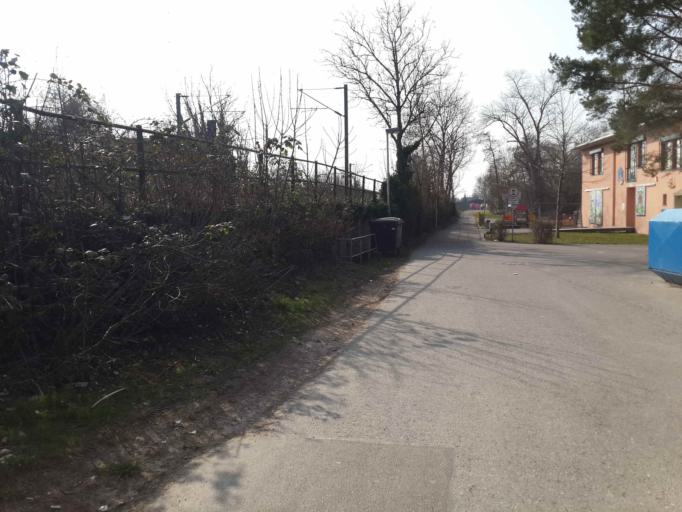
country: DE
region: Baden-Wuerttemberg
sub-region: Regierungsbezirk Stuttgart
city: Leingarten
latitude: 49.1451
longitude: 9.1271
